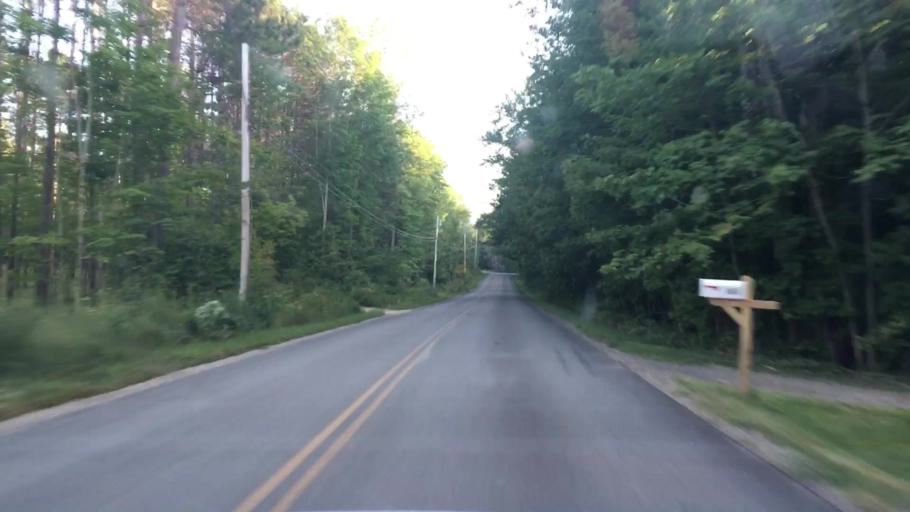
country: US
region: Maine
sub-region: Penobscot County
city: Hampden
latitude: 44.7079
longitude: -68.8882
